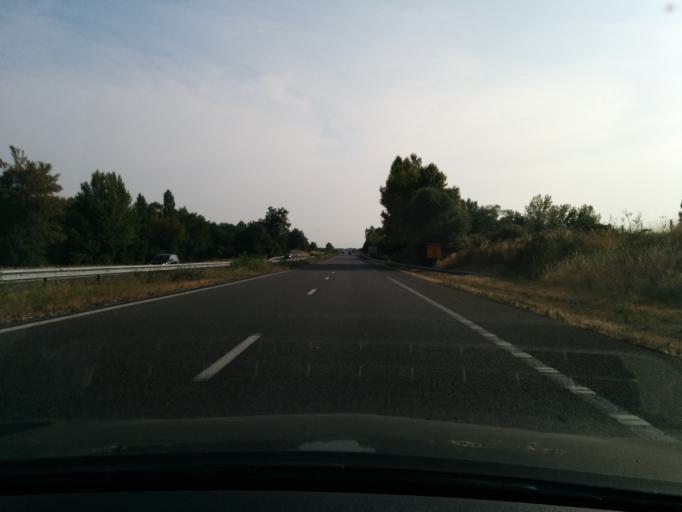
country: FR
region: Midi-Pyrenees
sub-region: Departement du Tarn
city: Lisle-sur-Tarn
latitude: 43.8347
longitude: 1.8327
